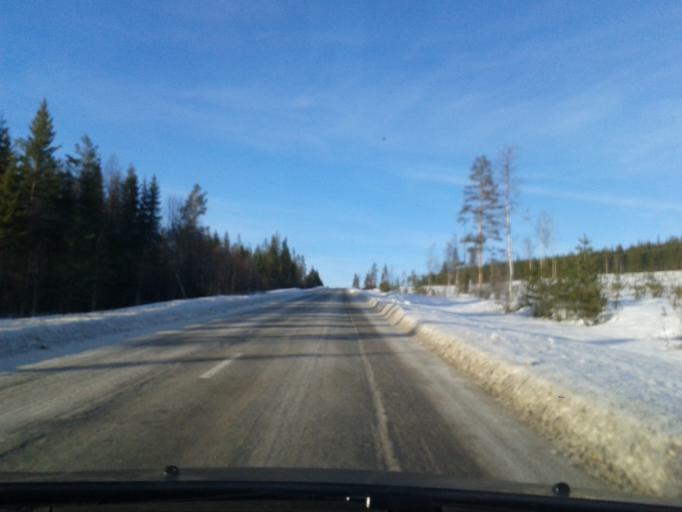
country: SE
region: Vaesternorrland
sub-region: OErnskoeldsviks Kommun
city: Bredbyn
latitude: 63.7662
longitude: 17.6852
